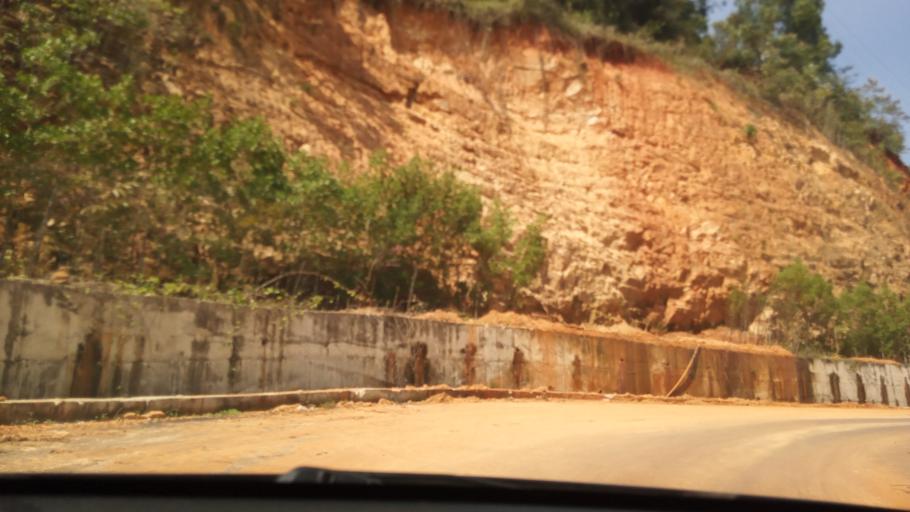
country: IN
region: Andhra Pradesh
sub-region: Chittoor
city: Tirumala
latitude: 13.6818
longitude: 79.3398
